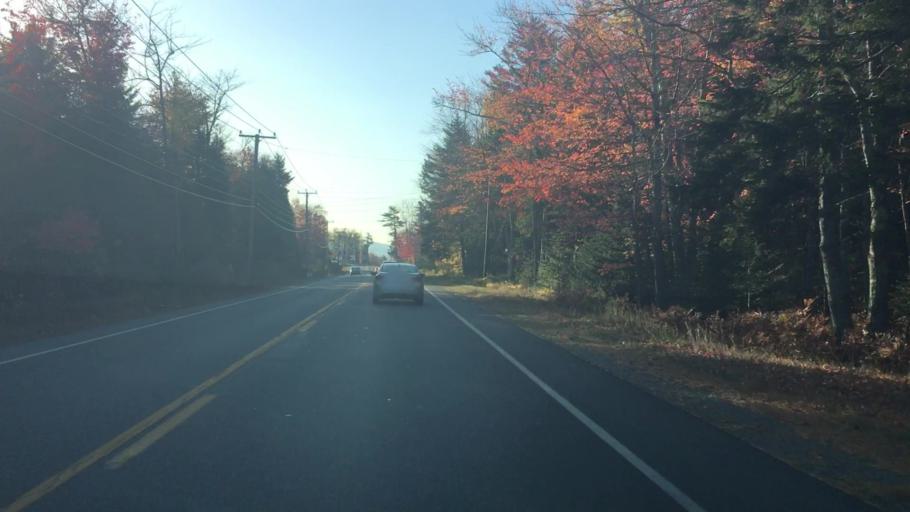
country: US
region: Maine
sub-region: Hancock County
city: Ellsworth
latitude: 44.5116
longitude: -68.3928
